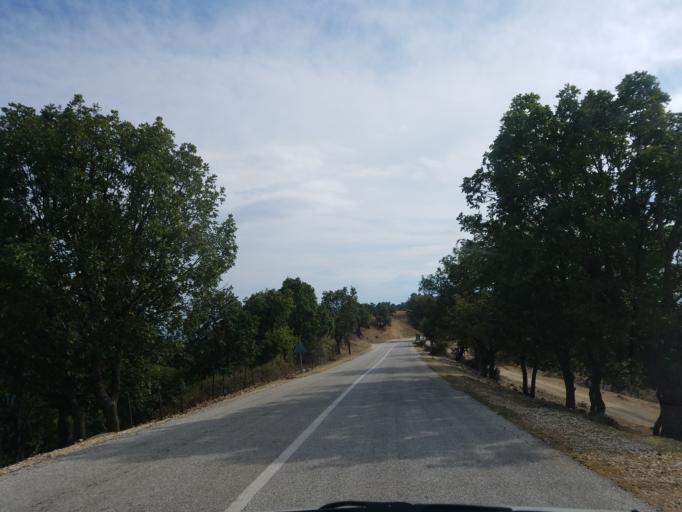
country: GR
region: Thessaly
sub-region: Trikala
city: Kastraki
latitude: 39.7587
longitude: 21.6636
